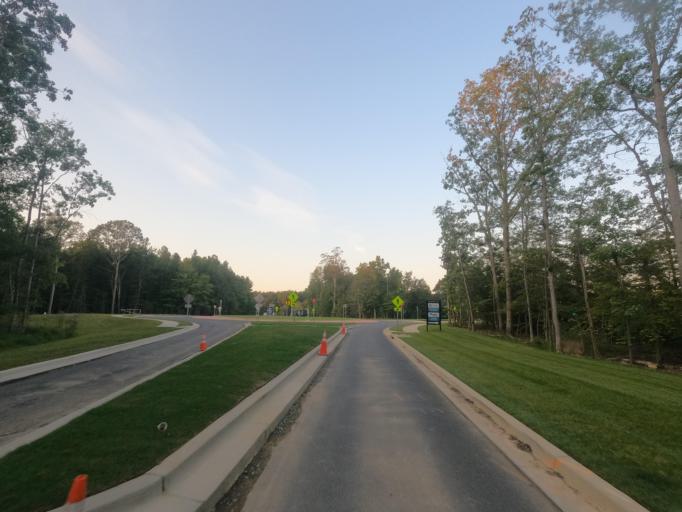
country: US
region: Maryland
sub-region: Prince George's County
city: Accokeek
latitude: 38.6609
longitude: -77.0107
